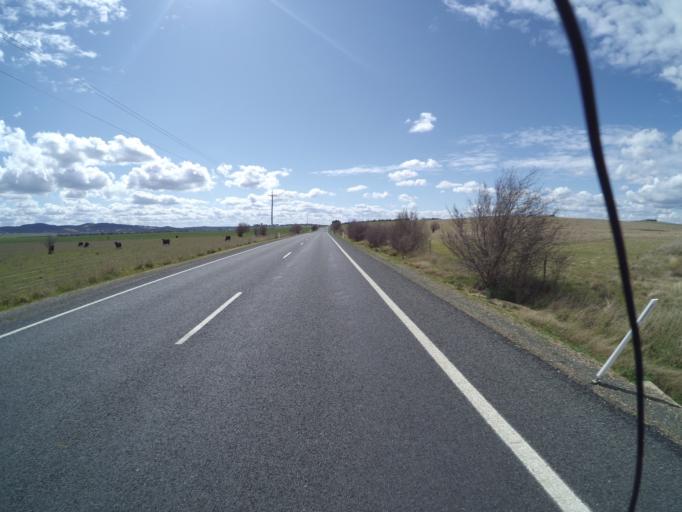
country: AU
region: New South Wales
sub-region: Goulburn Mulwaree
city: Goulburn
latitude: -34.8544
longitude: 149.6835
